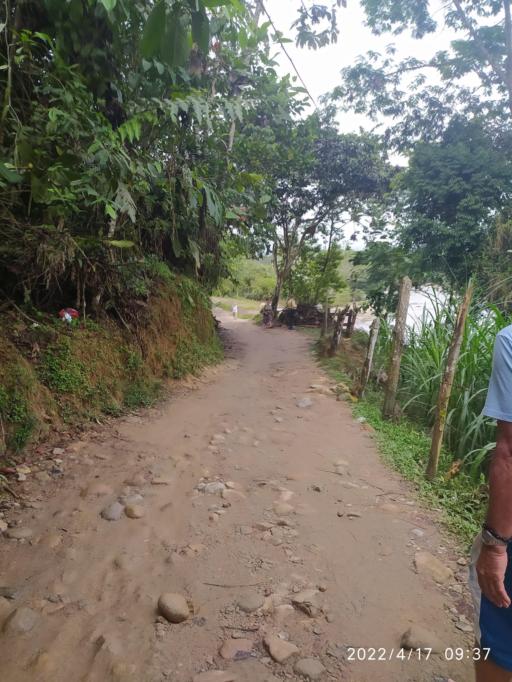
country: CO
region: Antioquia
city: San Carlos
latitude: 6.1859
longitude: -74.9892
